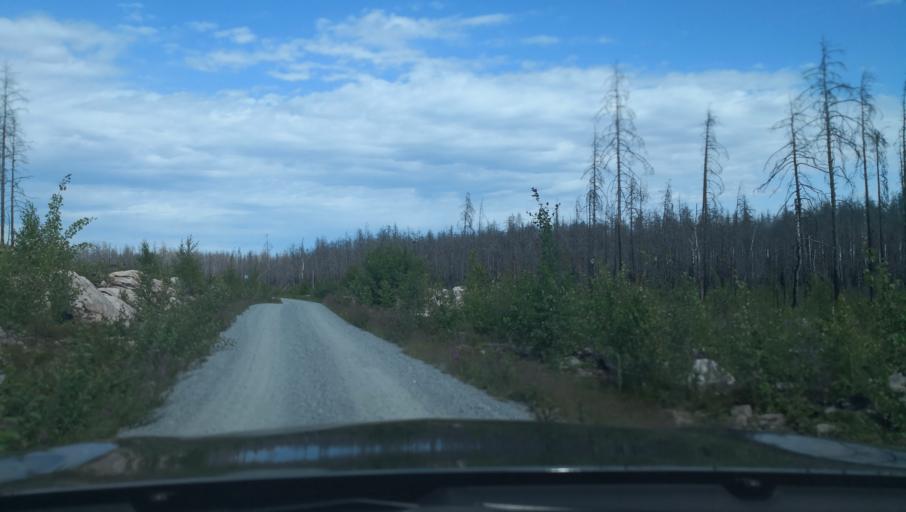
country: SE
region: Vaestmanland
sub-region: Surahammars Kommun
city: Ramnas
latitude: 59.9213
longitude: 16.1656
